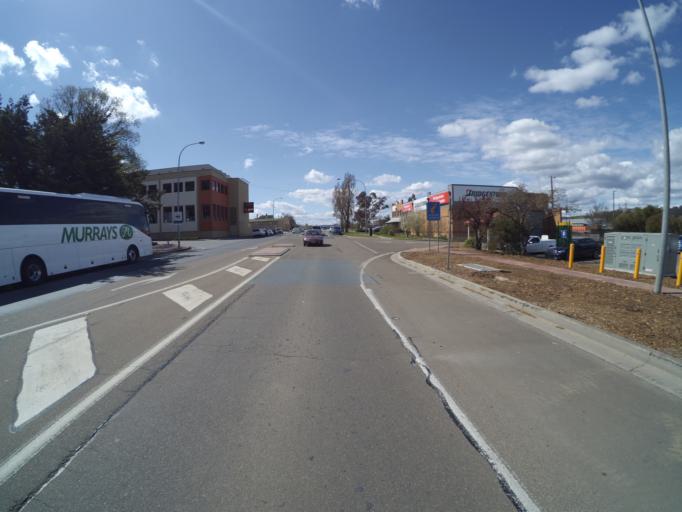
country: AU
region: New South Wales
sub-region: Goulburn Mulwaree
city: Goulburn
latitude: -34.7553
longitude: 149.7210
